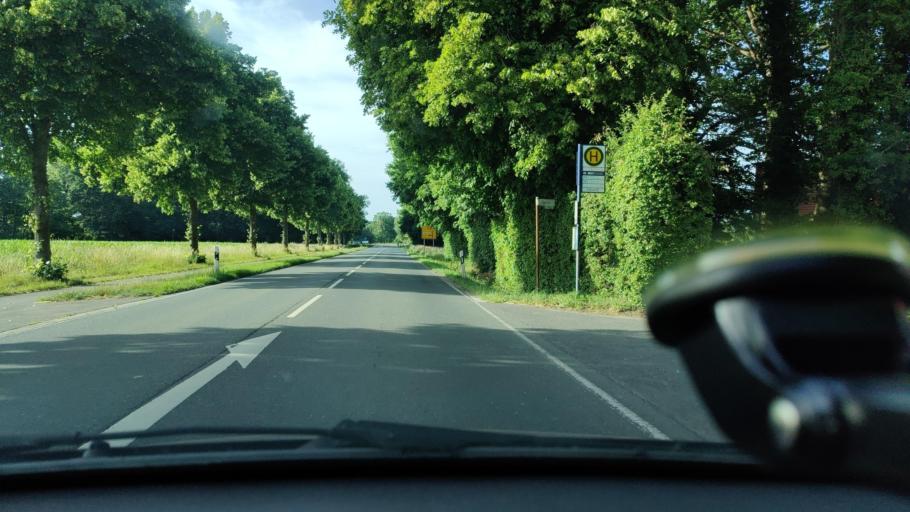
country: DE
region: North Rhine-Westphalia
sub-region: Regierungsbezirk Munster
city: Coesfeld
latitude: 51.9785
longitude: 7.1921
